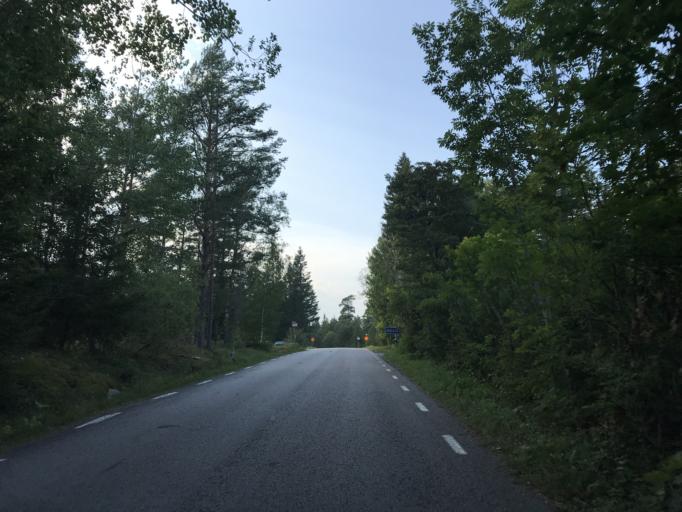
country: SE
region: Stockholm
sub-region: Norrtalje Kommun
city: Bjorko
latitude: 59.8653
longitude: 19.0321
